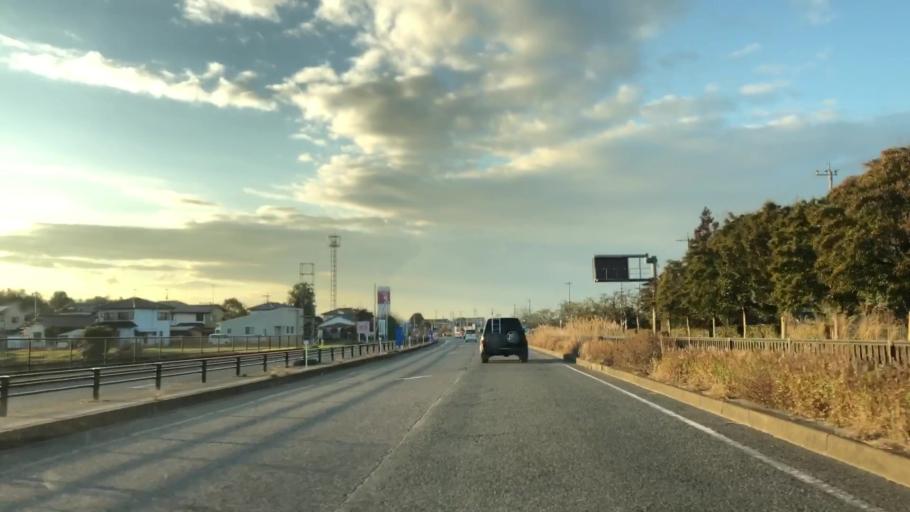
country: JP
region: Fukuoka
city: Nakatsu
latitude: 33.5594
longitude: 131.1983
